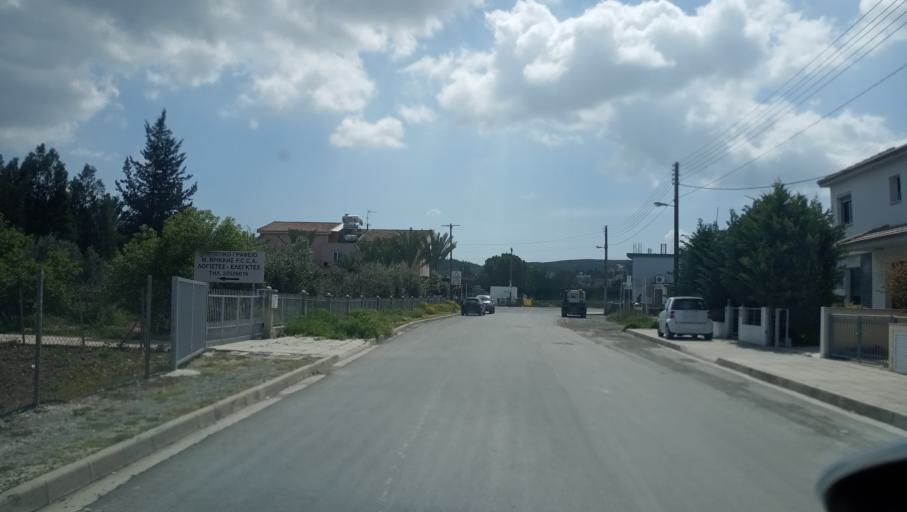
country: CY
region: Lefkosia
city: Dali
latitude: 35.0163
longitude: 33.3986
